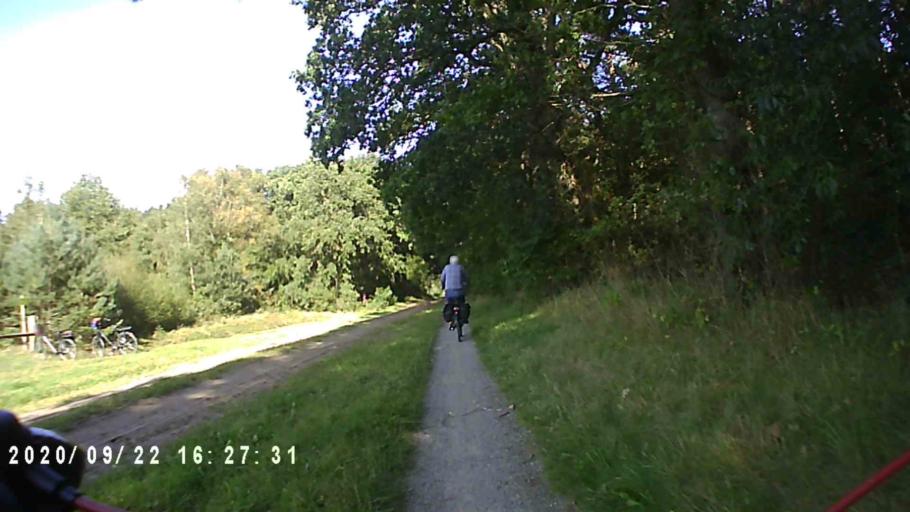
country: NL
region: Groningen
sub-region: Gemeente Leek
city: Leek
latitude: 53.0794
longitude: 6.4361
